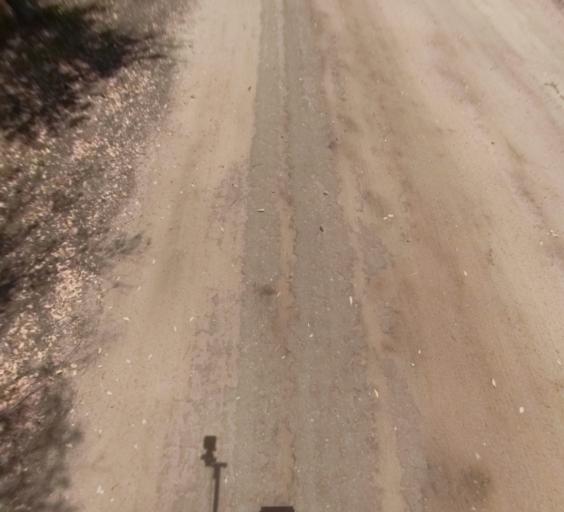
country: US
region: California
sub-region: Madera County
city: Madera Acres
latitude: 37.0467
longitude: -119.9832
